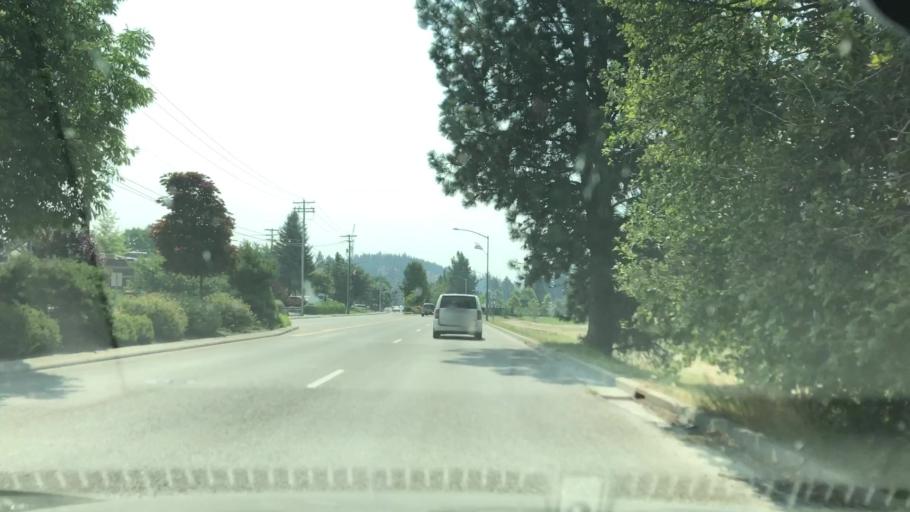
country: US
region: Idaho
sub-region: Kootenai County
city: Coeur d'Alene
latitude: 47.6819
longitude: -116.7933
